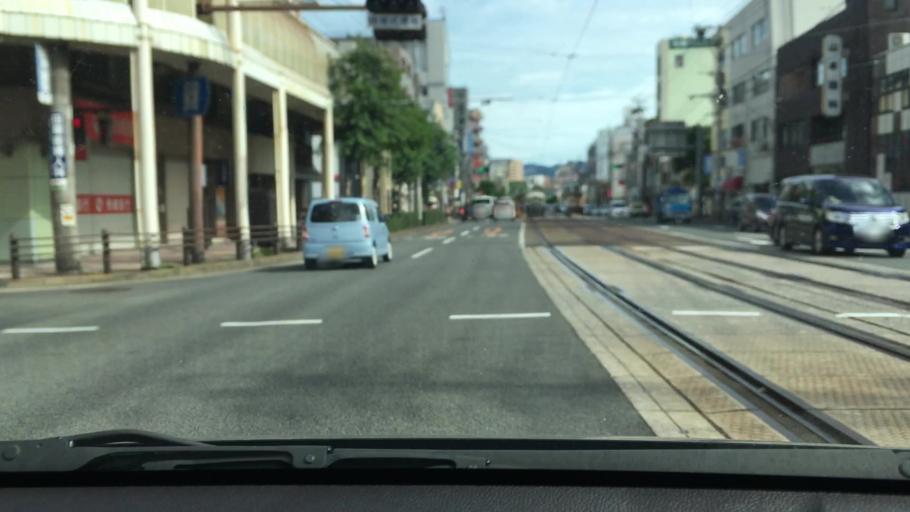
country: JP
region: Nagasaki
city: Obita
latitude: 32.7906
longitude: 129.8607
